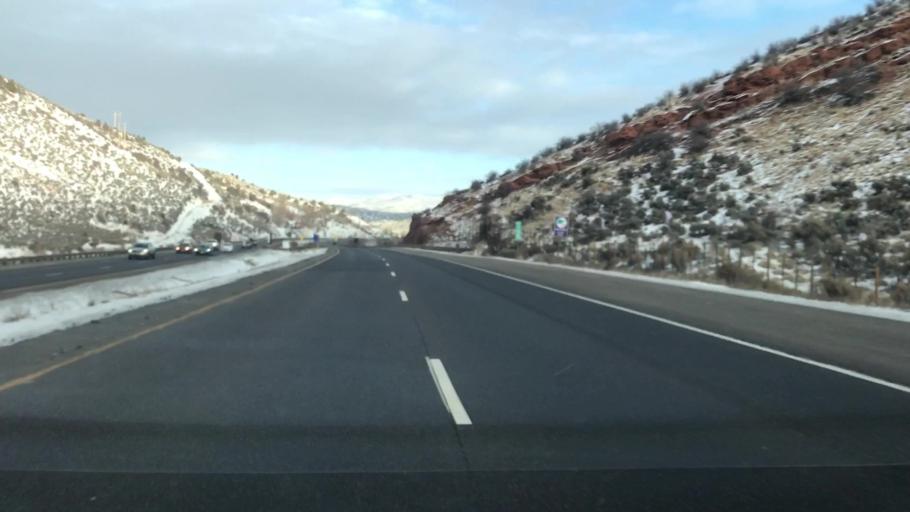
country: US
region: Colorado
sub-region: Eagle County
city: Edwards
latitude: 39.6712
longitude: -106.6453
